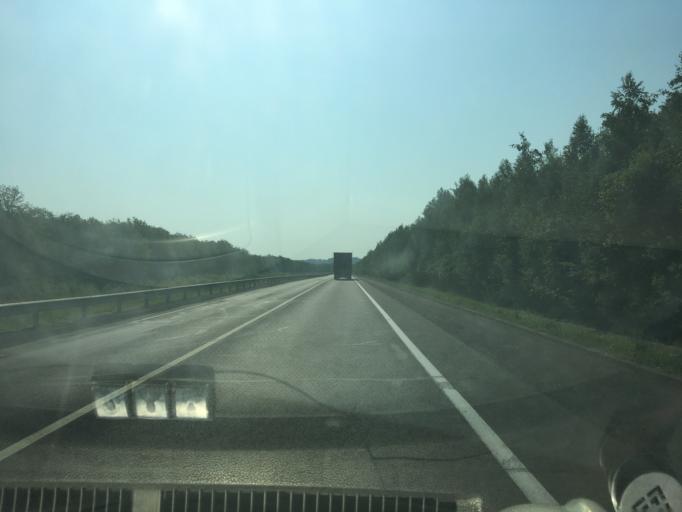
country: RU
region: Nizjnij Novgorod
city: Pamyat' Parizhskoy Kommuny
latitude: 56.0819
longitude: 44.3572
